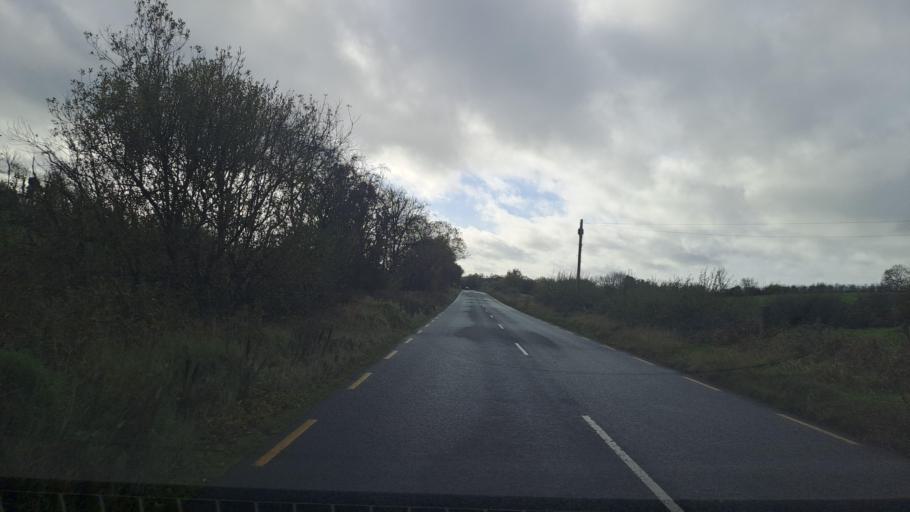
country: IE
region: Ulster
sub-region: County Monaghan
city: Monaghan
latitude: 54.1691
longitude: -6.9982
